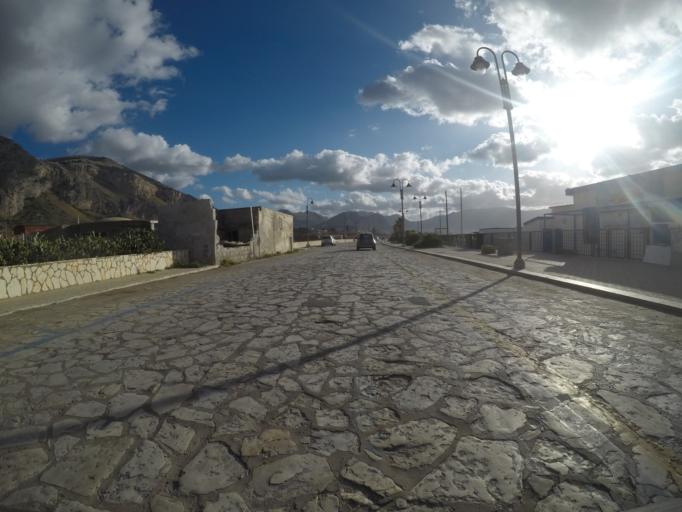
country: IT
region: Sicily
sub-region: Palermo
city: Isola delle Femmine
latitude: 38.1916
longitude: 13.2437
